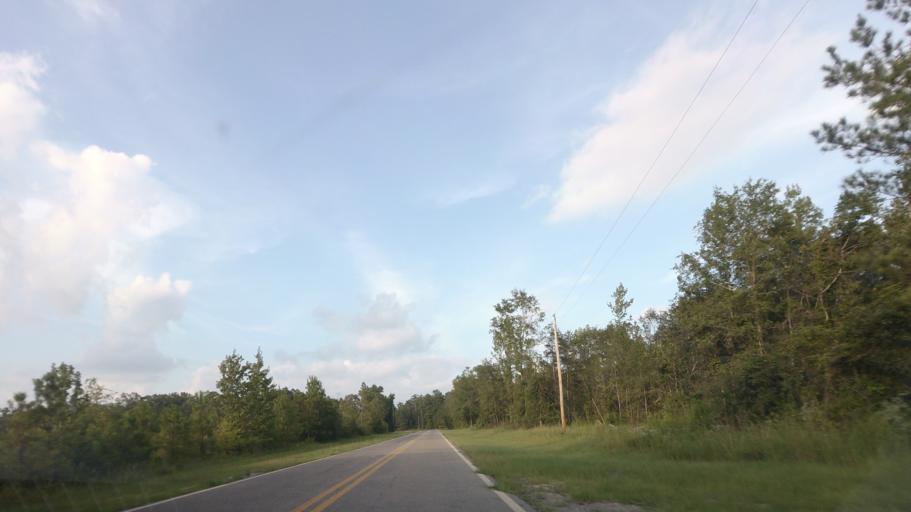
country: US
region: Georgia
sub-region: Wilkinson County
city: Gordon
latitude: 32.8347
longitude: -83.4125
